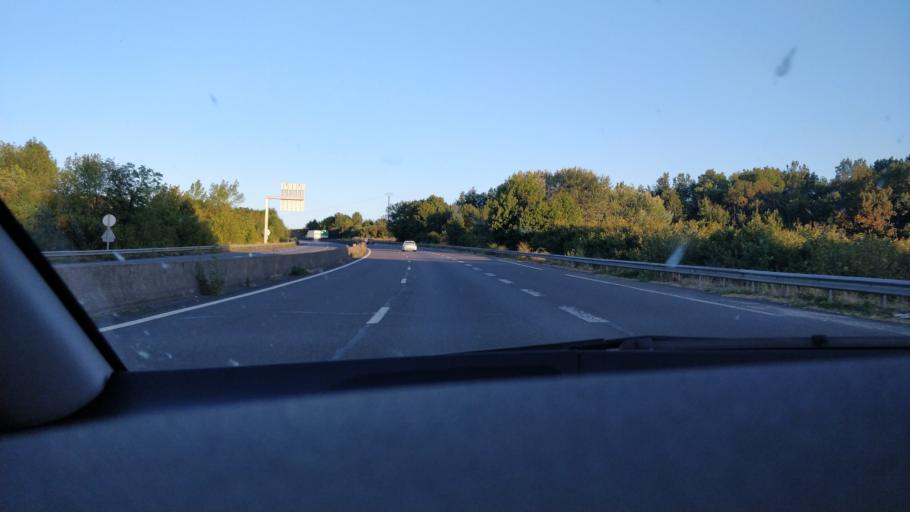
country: FR
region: Poitou-Charentes
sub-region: Departement de la Charente
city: Champniers
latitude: 45.6884
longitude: 0.1944
